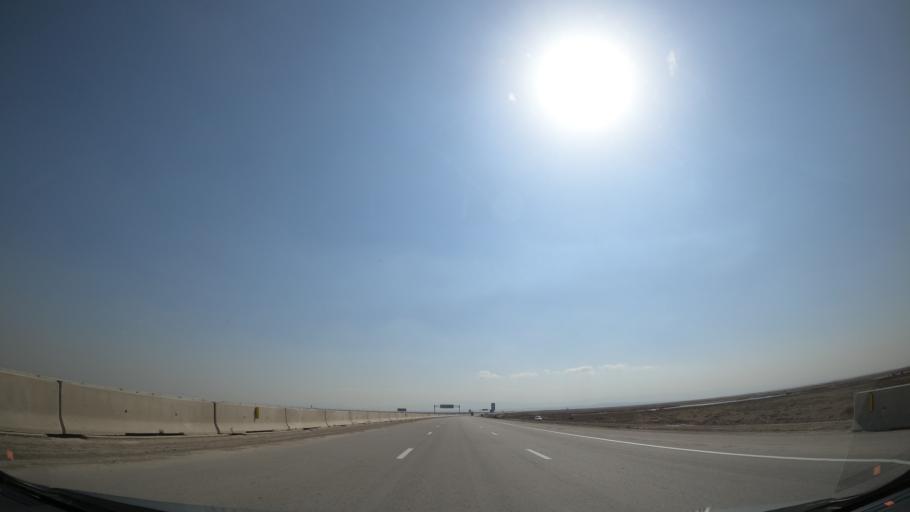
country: IR
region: Qazvin
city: Abyek
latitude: 35.9530
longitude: 50.4662
